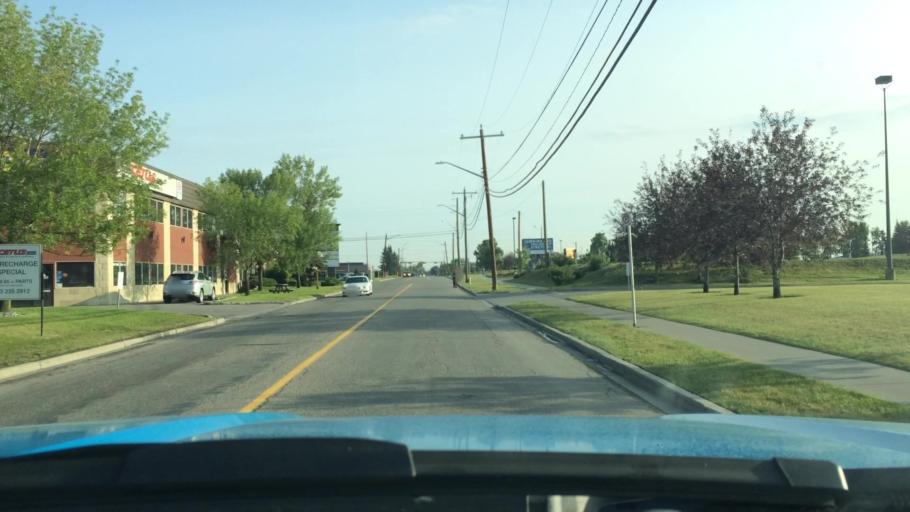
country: CA
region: Alberta
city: Calgary
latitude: 51.0786
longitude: -114.0051
